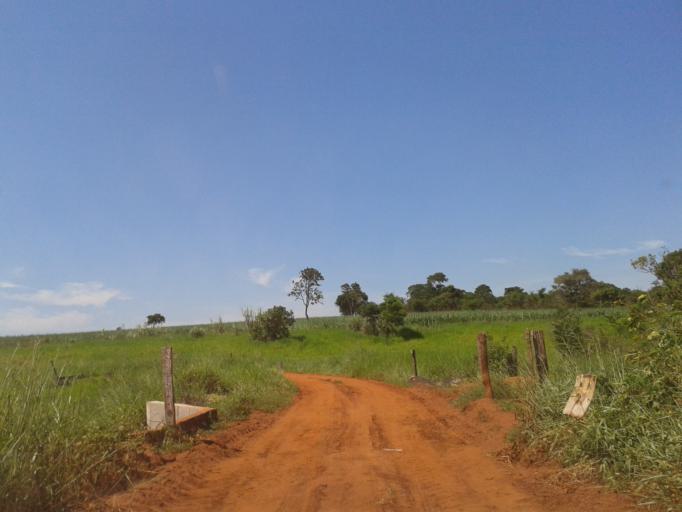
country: BR
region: Minas Gerais
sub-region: Santa Vitoria
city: Santa Vitoria
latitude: -19.0964
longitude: -50.4539
